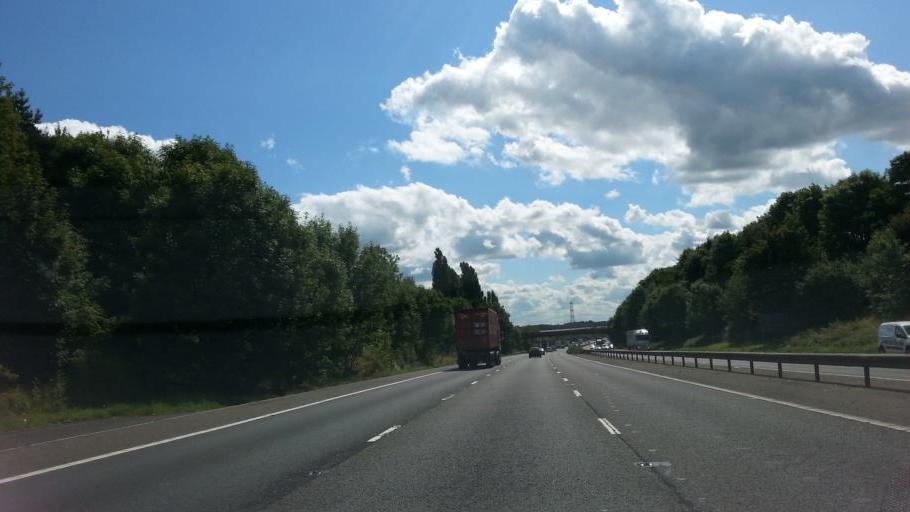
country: GB
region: England
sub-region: Leicestershire
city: Kirby Muxloe
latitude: 52.6520
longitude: -1.2380
